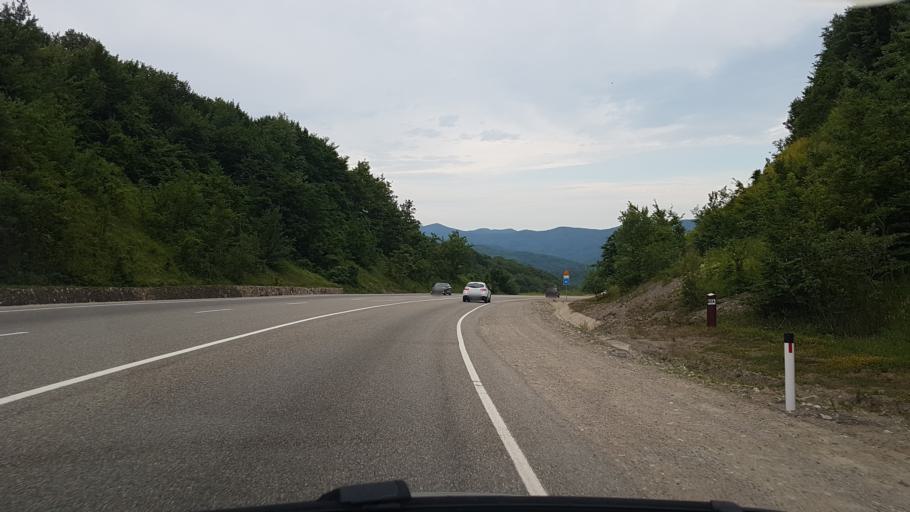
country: RU
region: Krasnodarskiy
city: Novomikhaylovskiy
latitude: 44.4986
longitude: 38.9055
